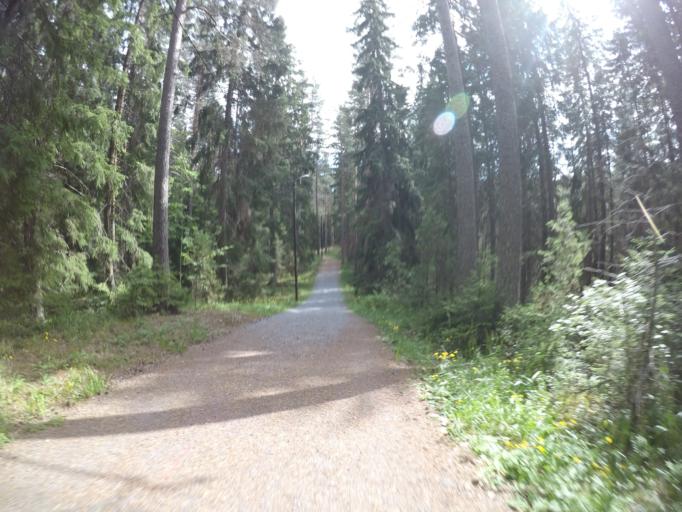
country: FI
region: Haeme
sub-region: Haemeenlinna
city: Haemeenlinna
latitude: 60.9980
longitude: 24.4064
